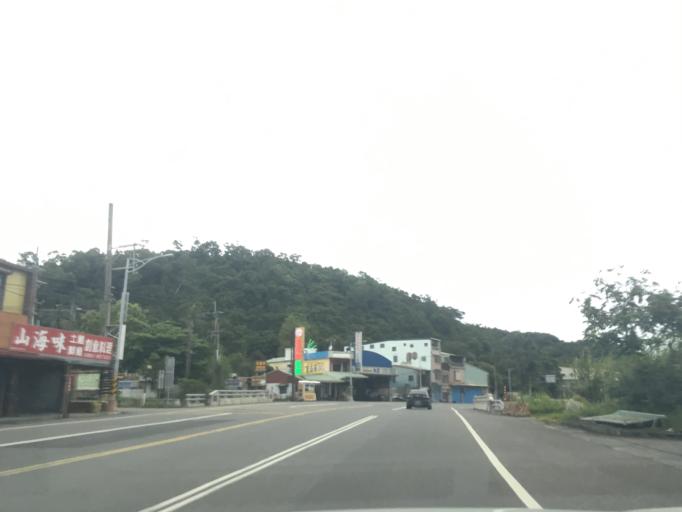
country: TW
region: Taiwan
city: Hengchun
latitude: 22.3406
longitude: 120.8933
